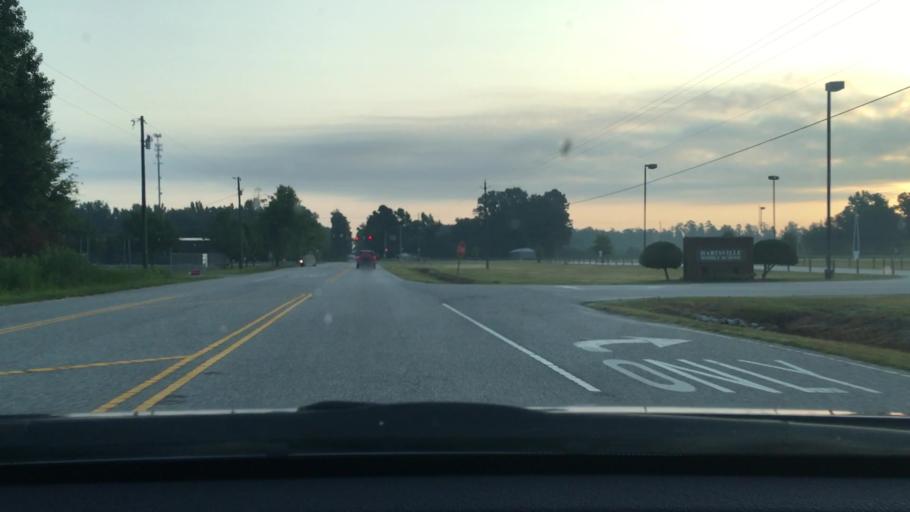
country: US
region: South Carolina
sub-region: Darlington County
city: Hartsville
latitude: 34.3424
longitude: -80.0983
